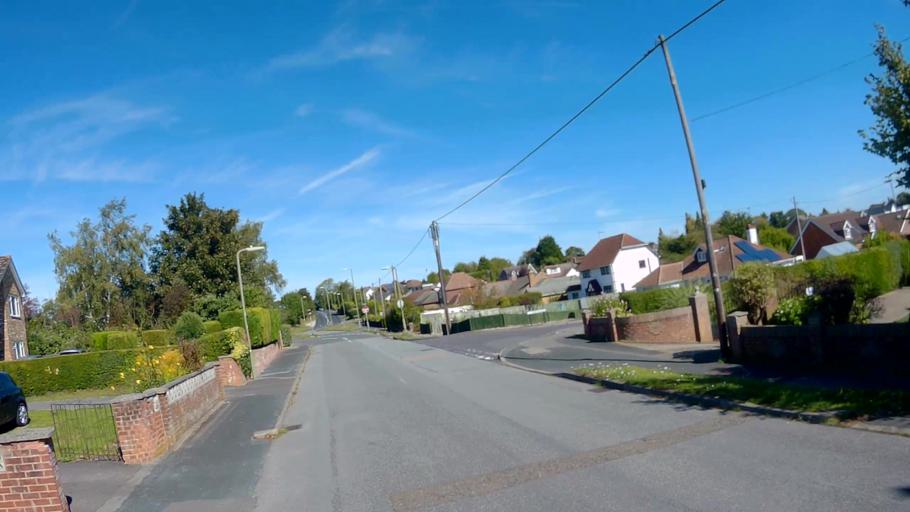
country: GB
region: England
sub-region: Hampshire
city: Basingstoke
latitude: 51.2645
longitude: -1.1333
